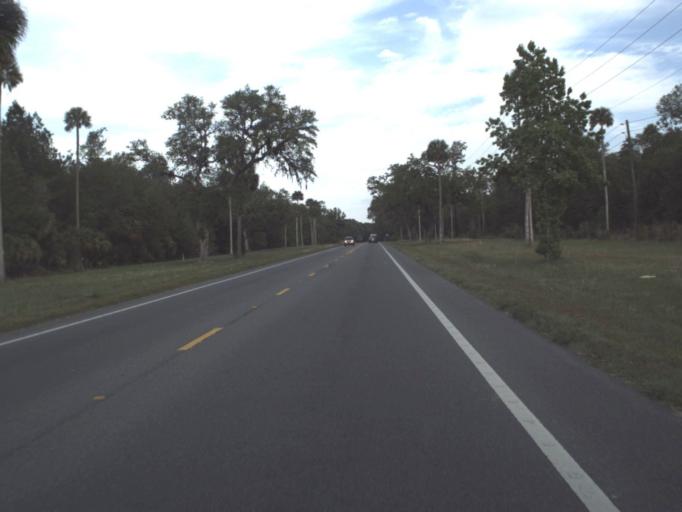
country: US
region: Florida
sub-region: Marion County
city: Silver Springs Shores
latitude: 29.2168
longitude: -82.0038
